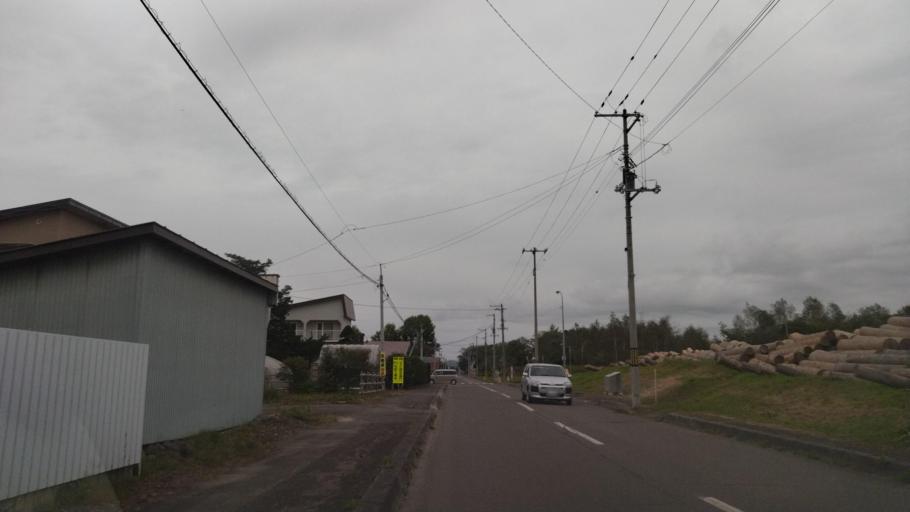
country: JP
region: Hokkaido
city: Otofuke
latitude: 43.2300
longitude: 143.2875
